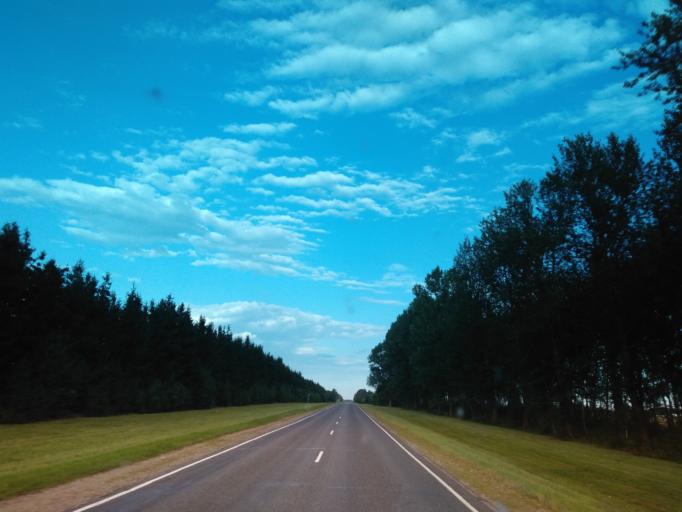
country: BY
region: Minsk
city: Uzda
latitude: 53.4389
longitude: 27.3089
